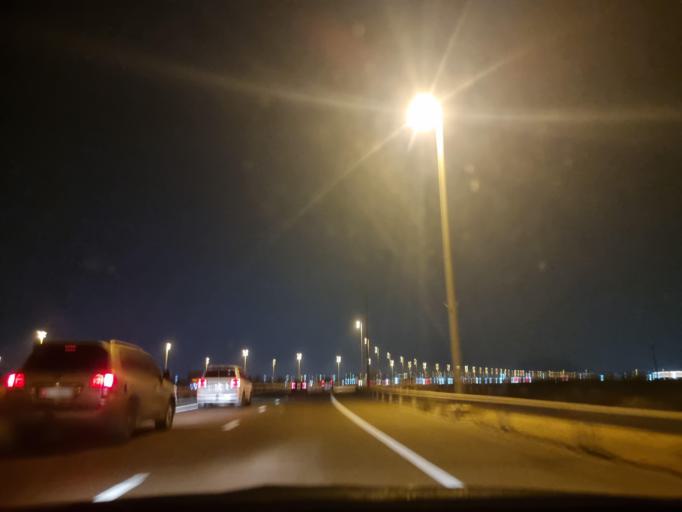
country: AE
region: Abu Dhabi
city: Abu Dhabi
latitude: 24.4114
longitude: 54.7140
